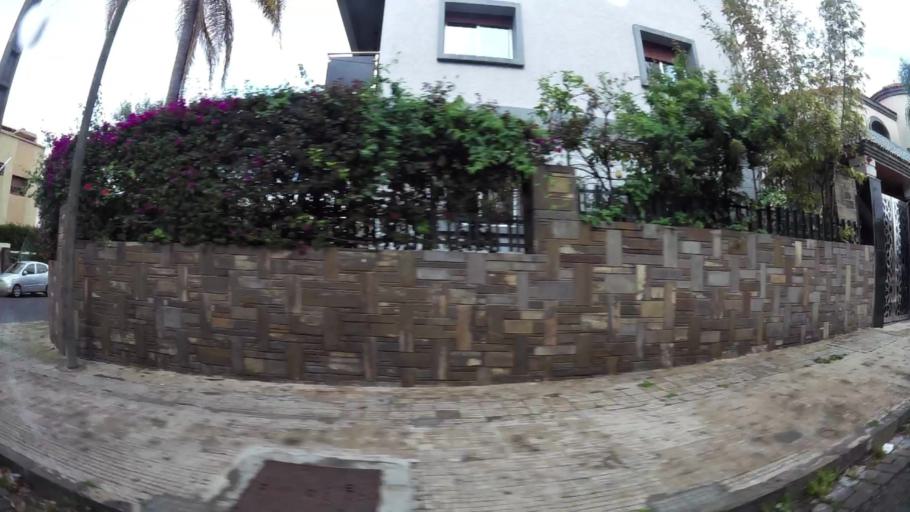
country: MA
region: Grand Casablanca
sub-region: Casablanca
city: Casablanca
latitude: 33.5530
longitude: -7.6078
